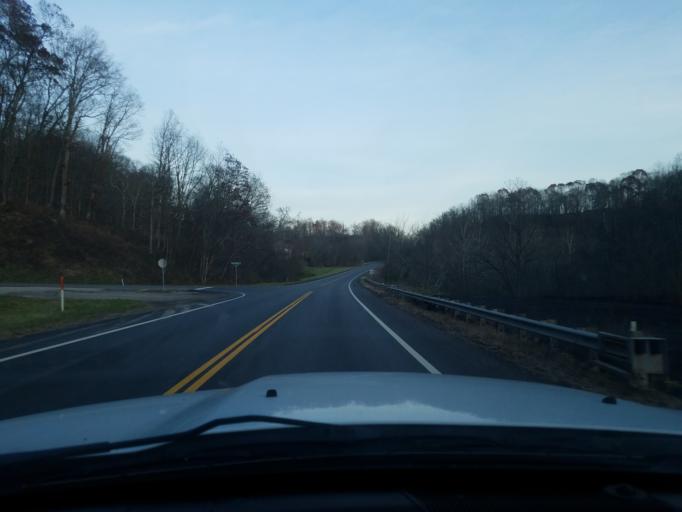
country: US
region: Ohio
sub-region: Washington County
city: Marietta
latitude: 39.4070
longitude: -81.4854
